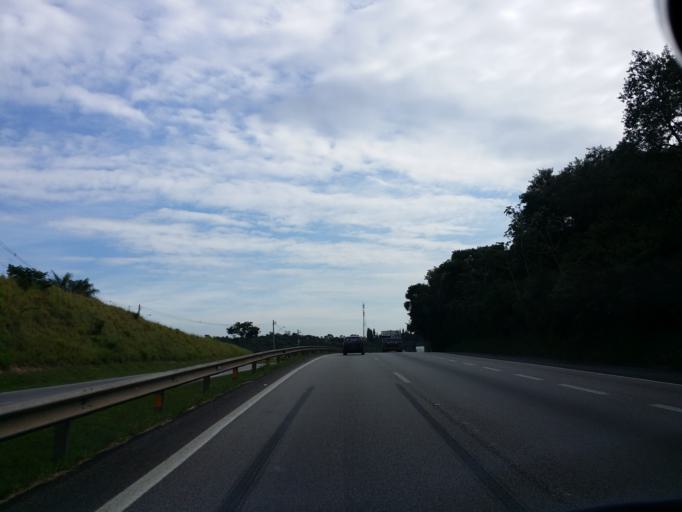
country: BR
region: Sao Paulo
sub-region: Itupeva
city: Itupeva
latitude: -23.1986
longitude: -46.9981
